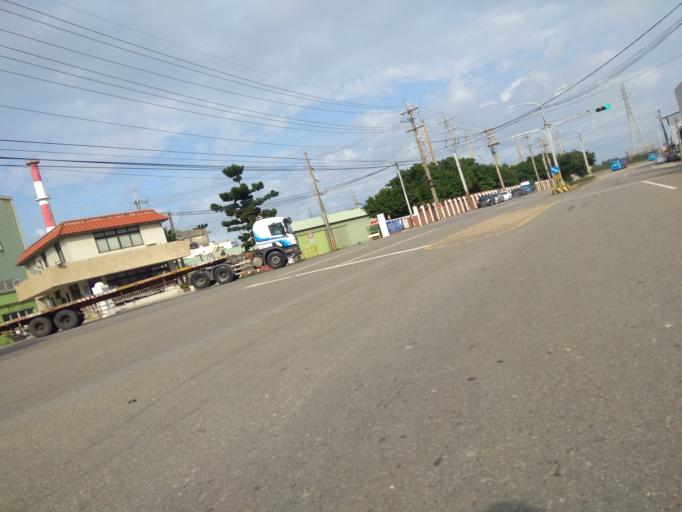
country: TW
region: Taiwan
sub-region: Hsinchu
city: Zhubei
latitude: 24.9816
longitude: 121.0268
